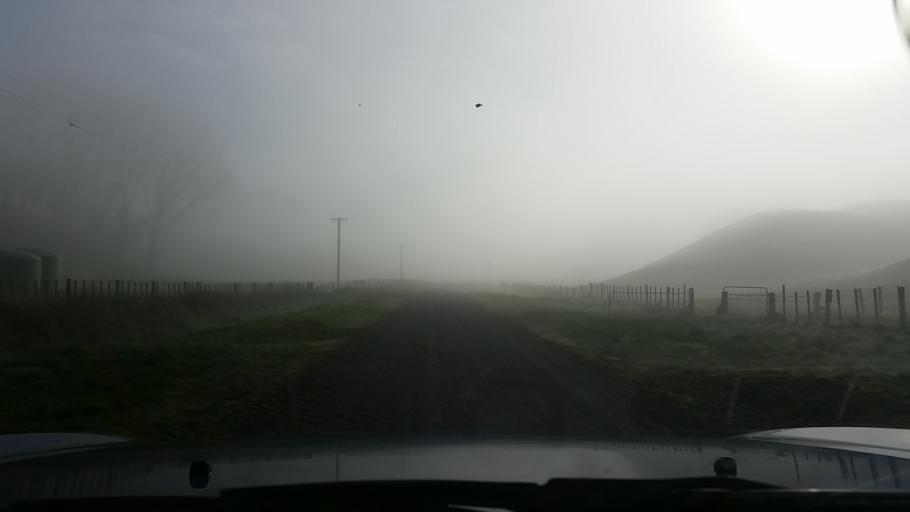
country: NZ
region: Bay of Plenty
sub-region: Rotorua District
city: Rotorua
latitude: -38.3136
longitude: 176.3022
